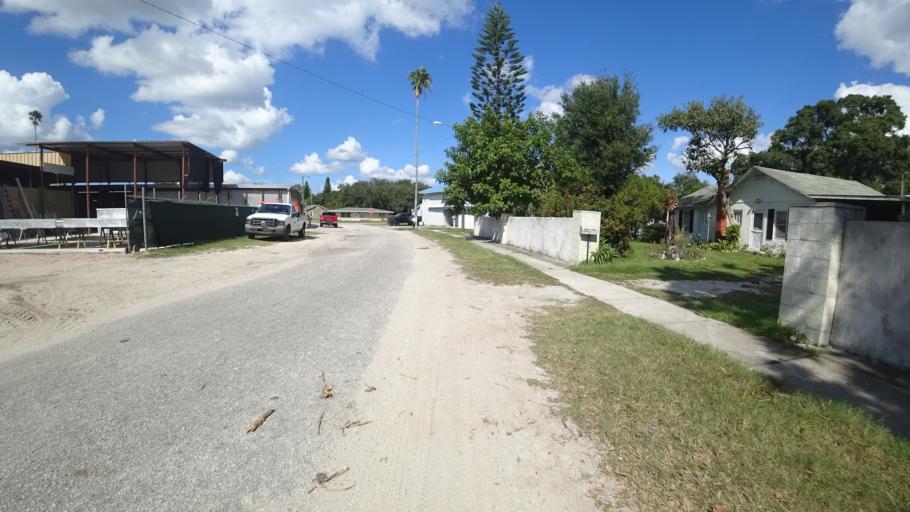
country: US
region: Florida
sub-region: Manatee County
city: South Bradenton
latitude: 27.4745
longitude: -82.5722
